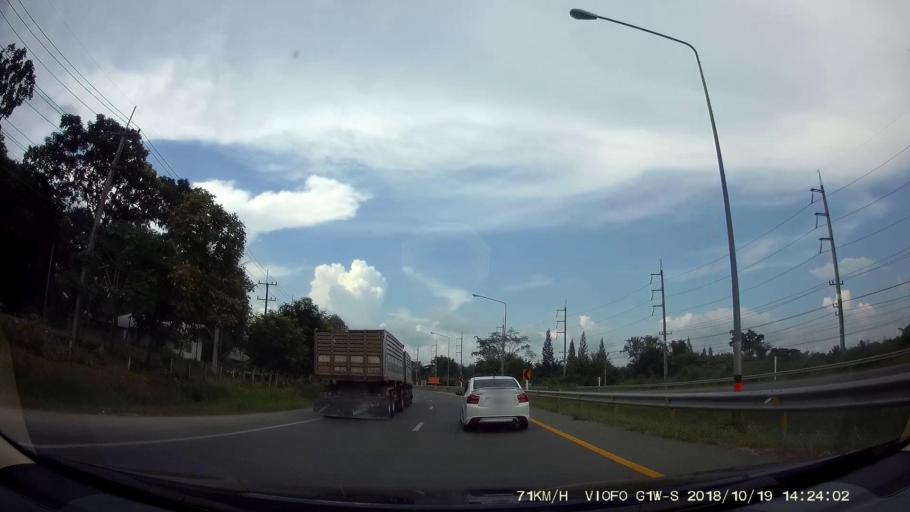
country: TH
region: Chaiyaphum
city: Kaeng Khro
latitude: 16.0770
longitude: 102.2768
